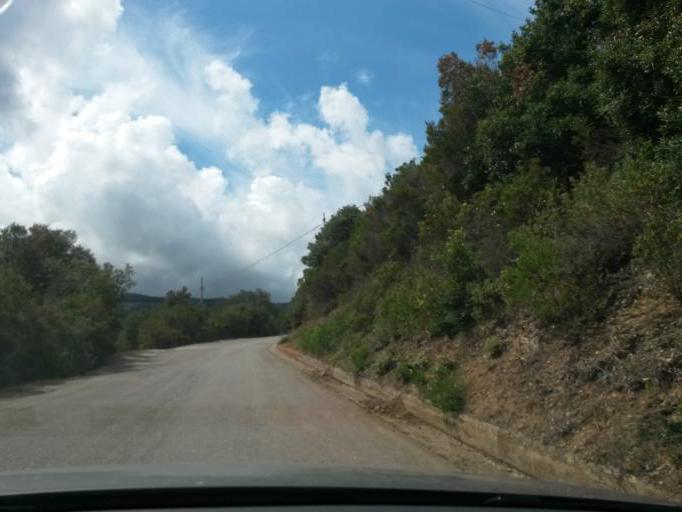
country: IT
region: Tuscany
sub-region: Provincia di Livorno
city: Porto Azzurro
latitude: 42.7548
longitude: 10.3975
